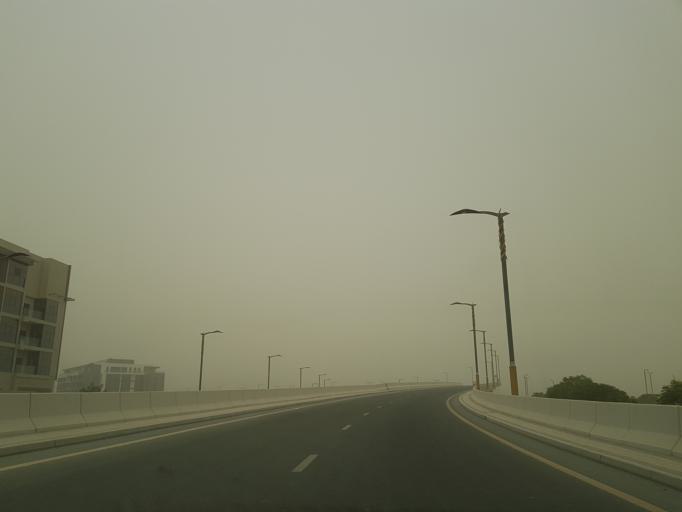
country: AE
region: Dubai
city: Dubai
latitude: 25.1560
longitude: 55.2935
